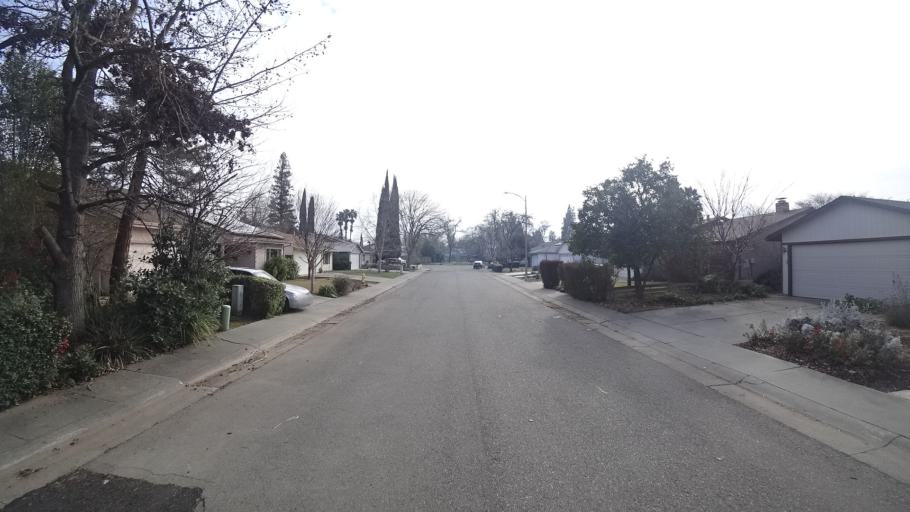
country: US
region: California
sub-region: Yolo County
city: Davis
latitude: 38.5454
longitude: -121.7168
